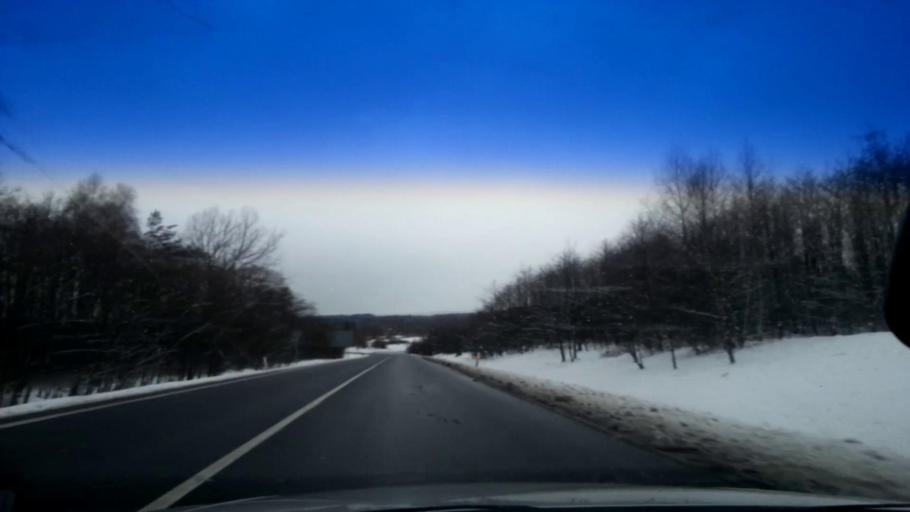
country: CZ
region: Karlovarsky
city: As
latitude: 50.1942
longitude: 12.2157
